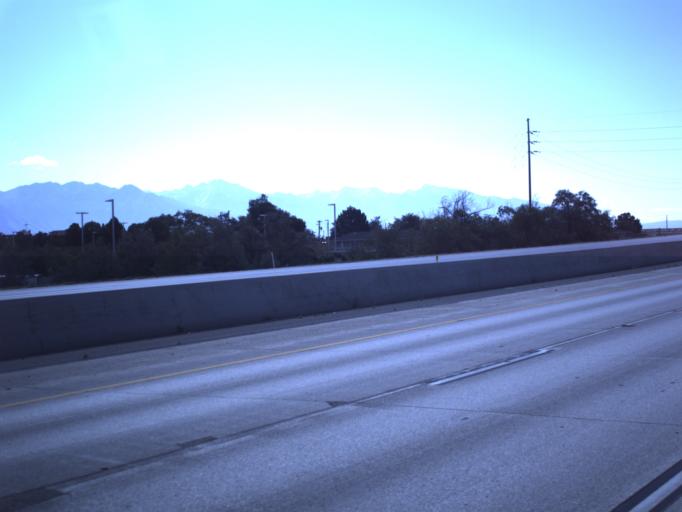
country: US
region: Utah
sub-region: Salt Lake County
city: Salt Lake City
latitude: 40.7742
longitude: -111.9494
